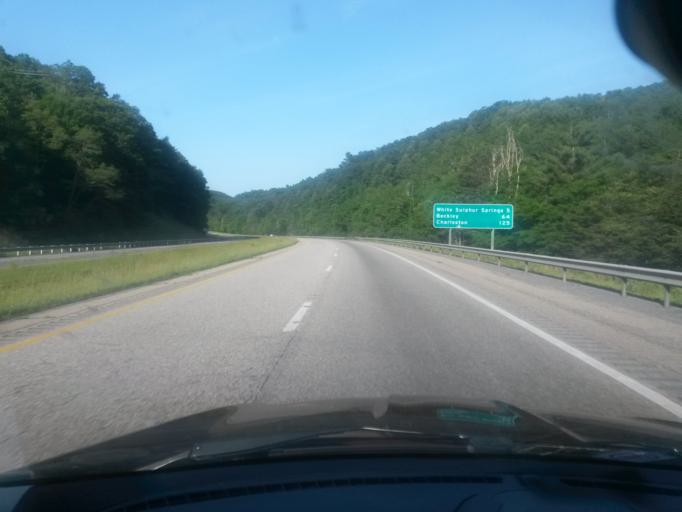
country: US
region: West Virginia
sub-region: Greenbrier County
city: White Sulphur Springs
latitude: 37.7991
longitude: -80.2087
